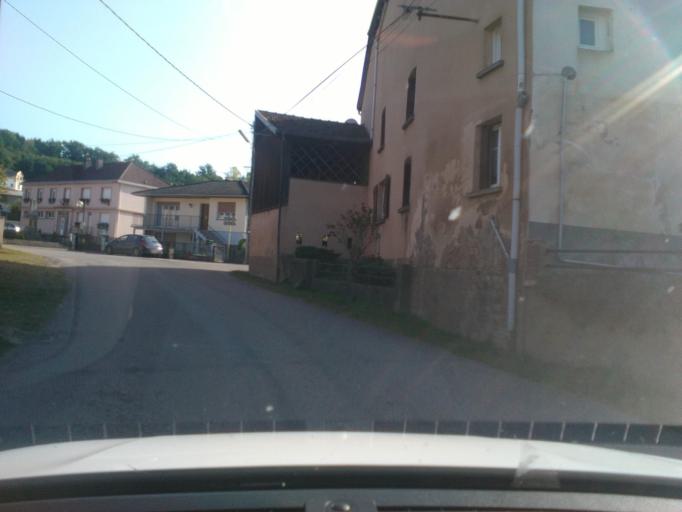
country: FR
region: Lorraine
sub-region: Departement des Vosges
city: Senones
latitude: 48.3961
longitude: 6.9987
